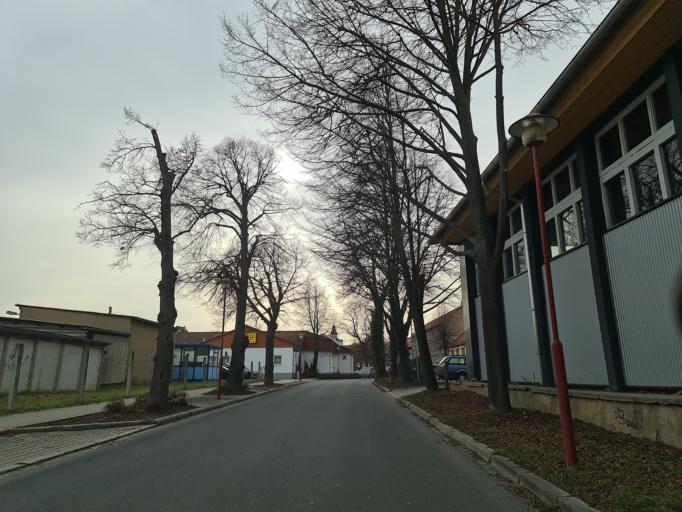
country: DE
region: Thuringia
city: Eisenberg
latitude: 50.9727
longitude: 11.8960
